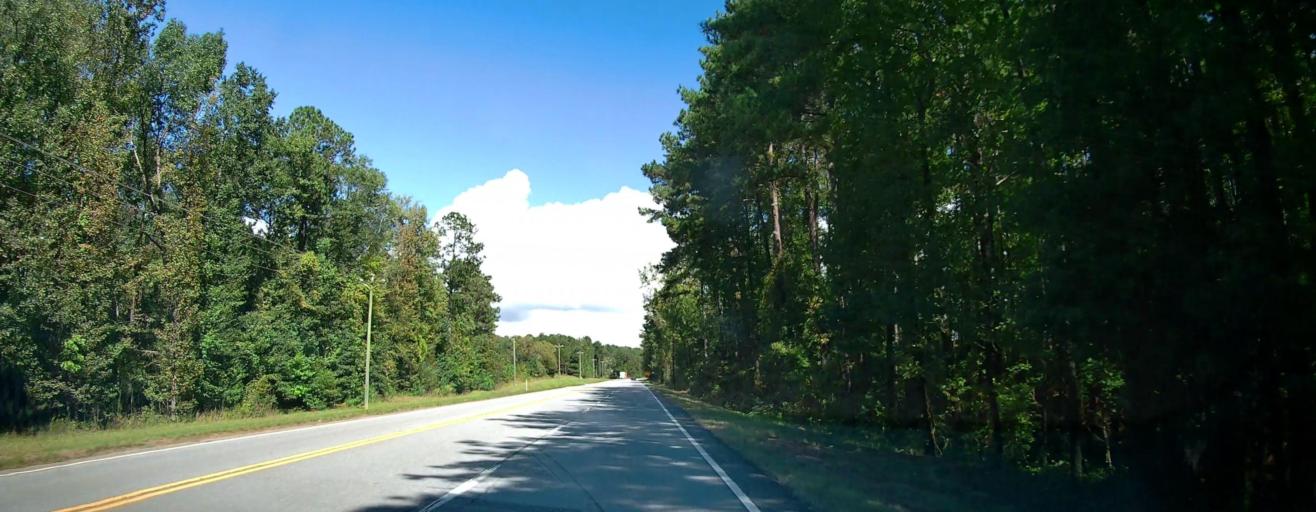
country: US
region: Georgia
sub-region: Jones County
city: Gray
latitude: 32.9353
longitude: -83.4978
